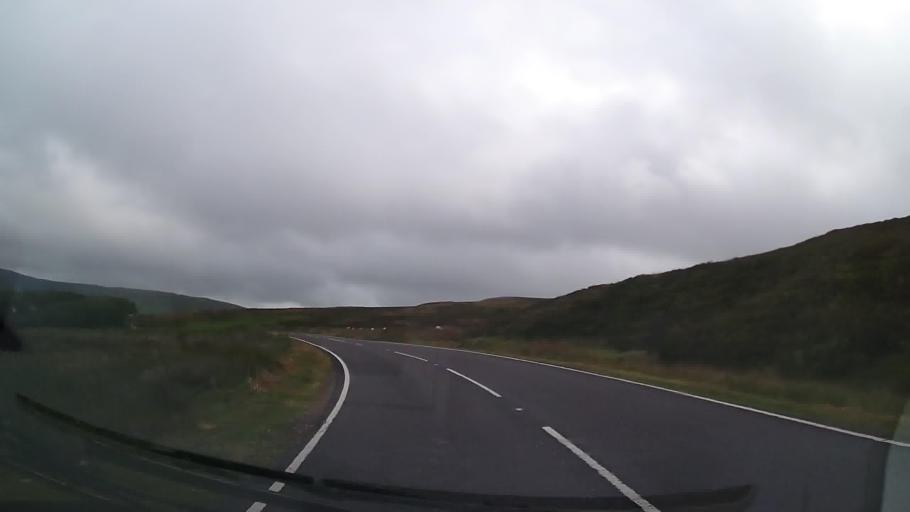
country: GB
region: Wales
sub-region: Denbighshire
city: Llandrillo
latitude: 52.8741
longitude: -3.4759
